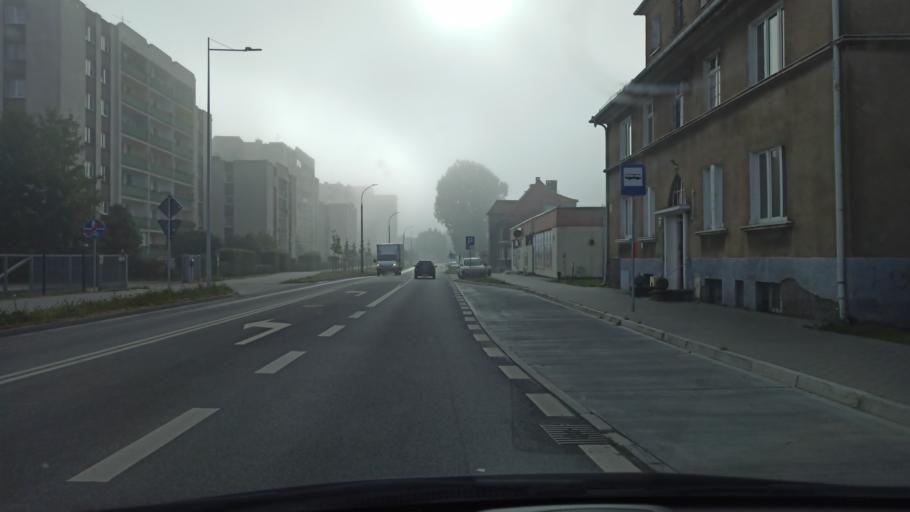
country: PL
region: Warmian-Masurian Voivodeship
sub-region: Powiat elblaski
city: Elblag
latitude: 54.1496
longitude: 19.4128
